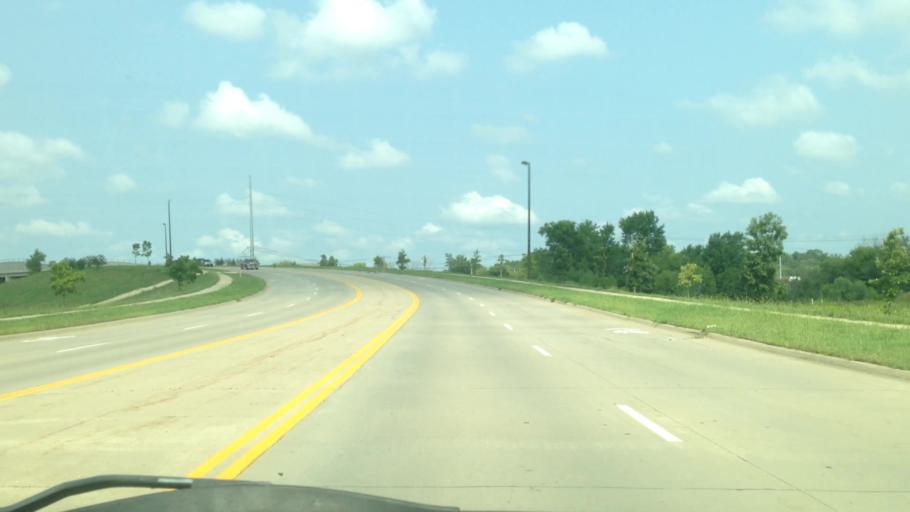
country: US
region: Iowa
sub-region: Linn County
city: Cedar Rapids
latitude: 41.9445
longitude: -91.6910
